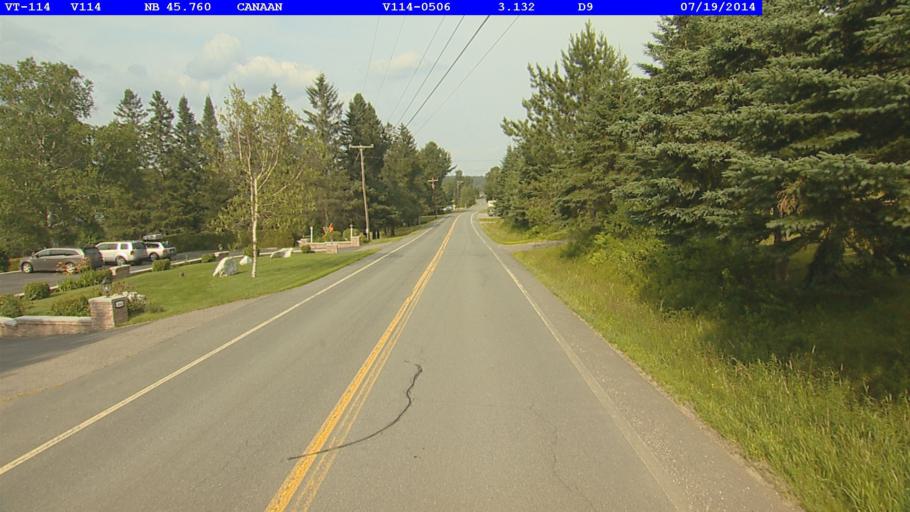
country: US
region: New Hampshire
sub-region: Coos County
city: Colebrook
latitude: 45.0090
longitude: -71.6311
